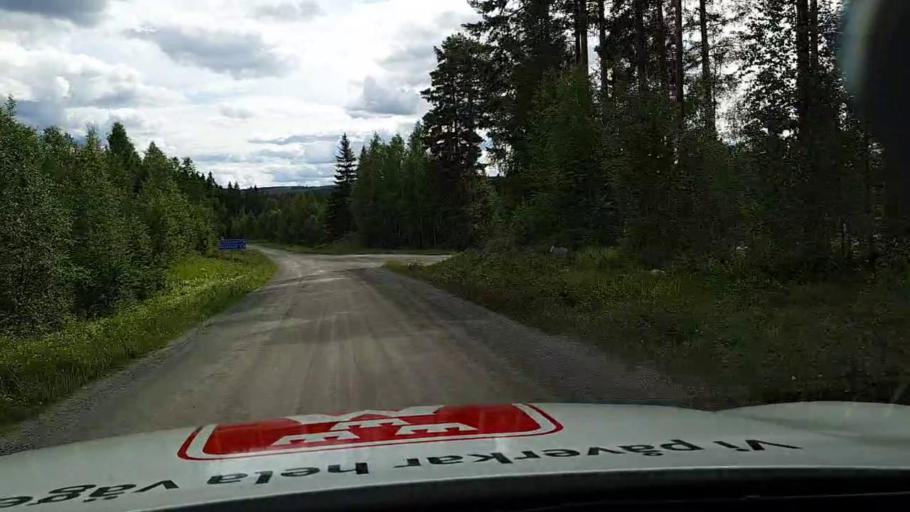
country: SE
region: Jaemtland
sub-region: Braecke Kommun
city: Braecke
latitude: 63.2223
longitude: 15.3453
